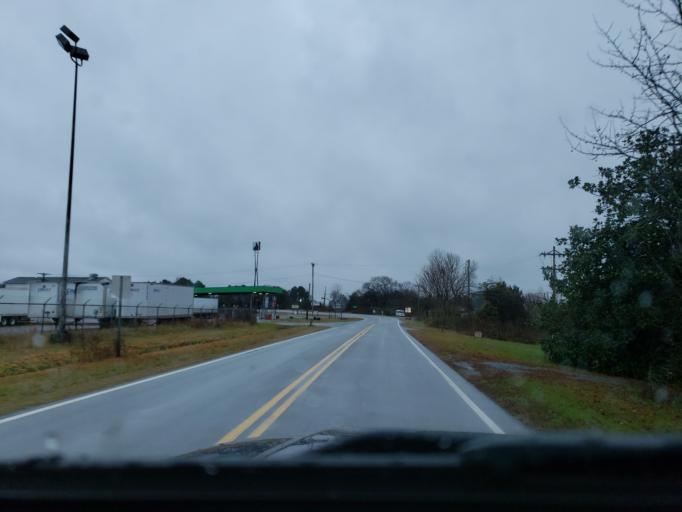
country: US
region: North Carolina
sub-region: Cleveland County
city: White Plains
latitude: 35.1967
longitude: -81.3716
